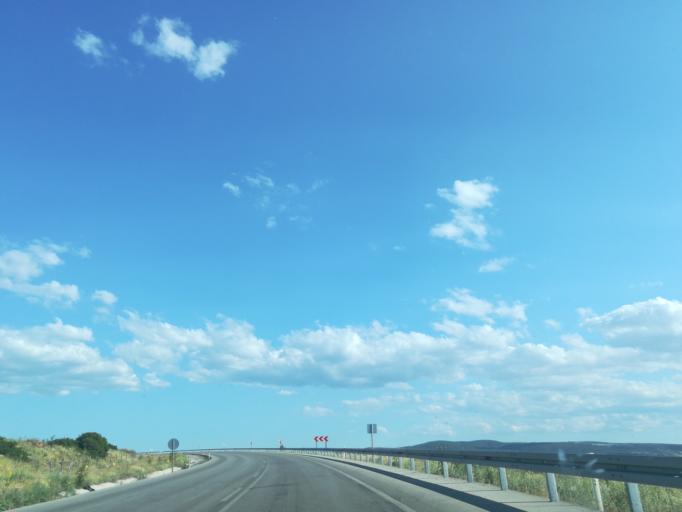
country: TR
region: Denizli
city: Ishakli
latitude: 38.1683
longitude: 30.0713
